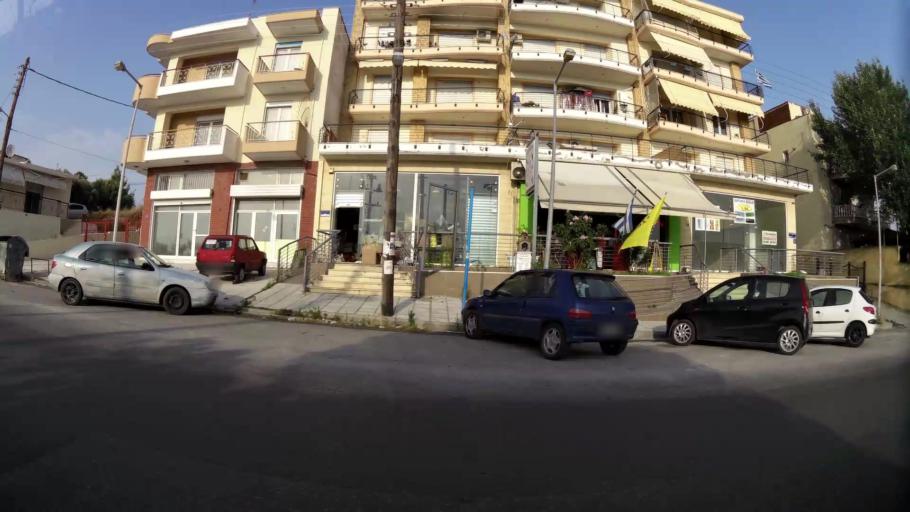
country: GR
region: Central Macedonia
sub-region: Nomos Thessalonikis
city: Evosmos
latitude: 40.6794
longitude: 22.9061
